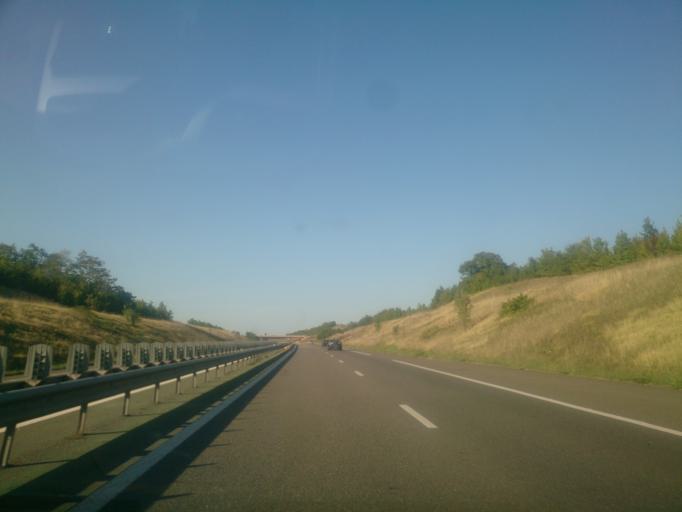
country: FR
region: Midi-Pyrenees
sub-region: Departement du Tarn-et-Garonne
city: Caussade
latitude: 44.1730
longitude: 1.5292
